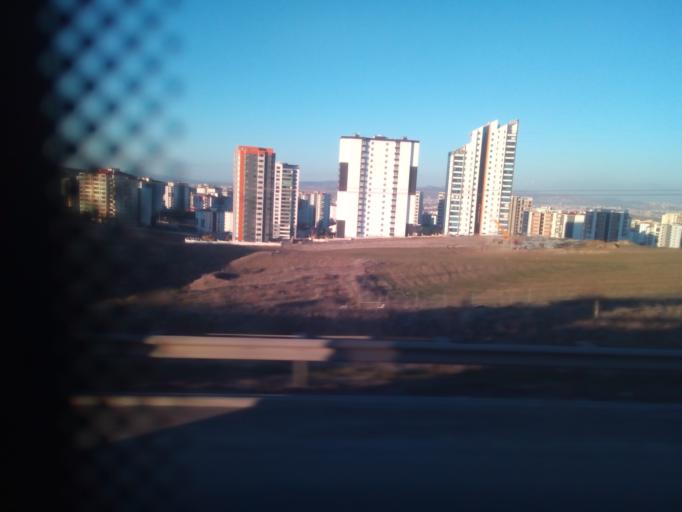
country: TR
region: Ankara
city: Etimesgut
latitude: 39.8798
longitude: 32.6250
